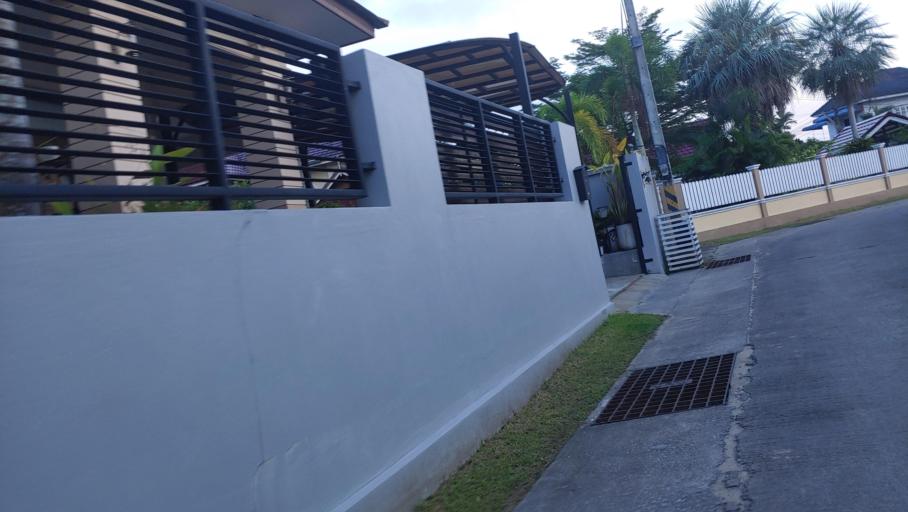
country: TH
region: Narathiwat
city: Narathiwat
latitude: 6.4404
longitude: 101.8177
